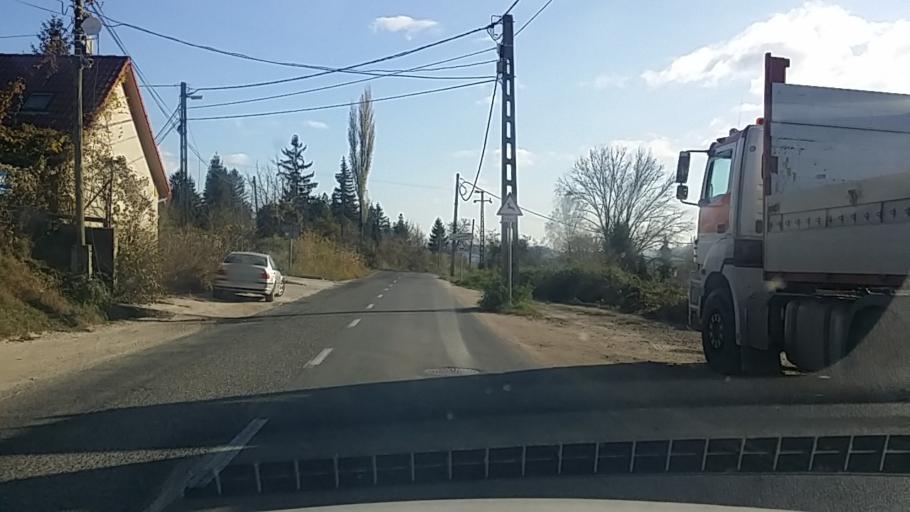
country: HU
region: Pest
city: Pilisszanto
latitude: 47.6622
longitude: 18.8942
